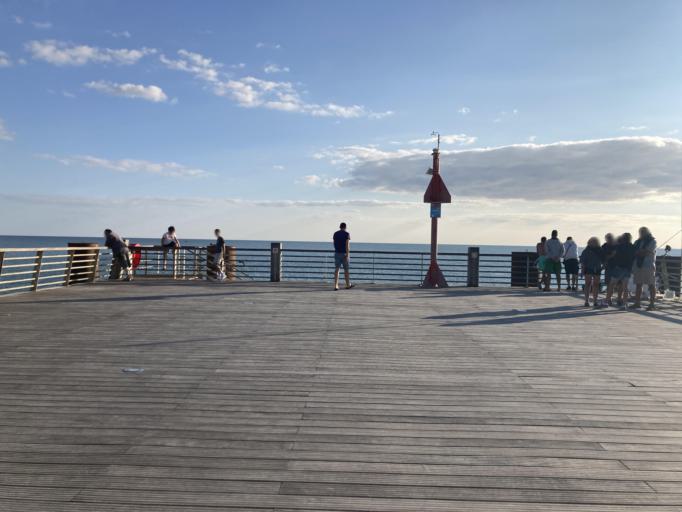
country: FR
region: Pays de la Loire
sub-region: Departement de la Vendee
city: Saint-Jean-de-Monts
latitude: 46.7847
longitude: -2.0851
